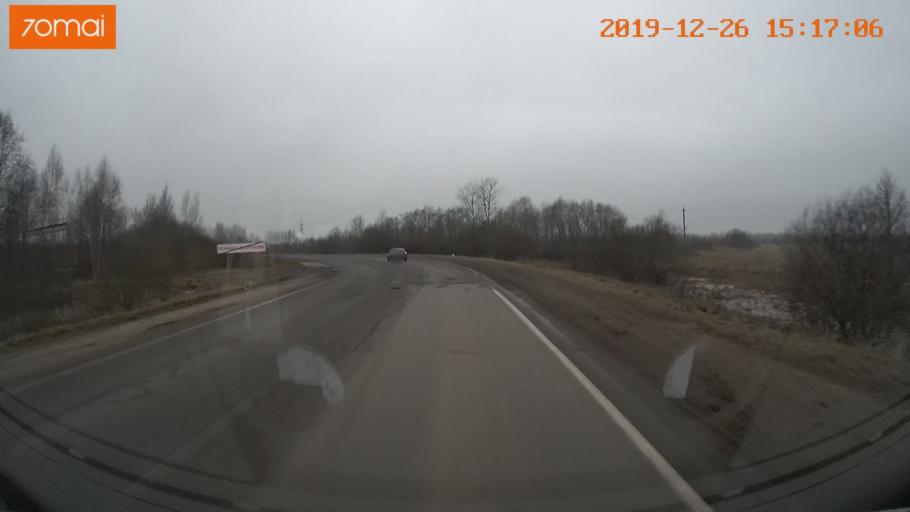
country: RU
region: Jaroslavl
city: Rybinsk
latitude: 58.0799
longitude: 38.8541
